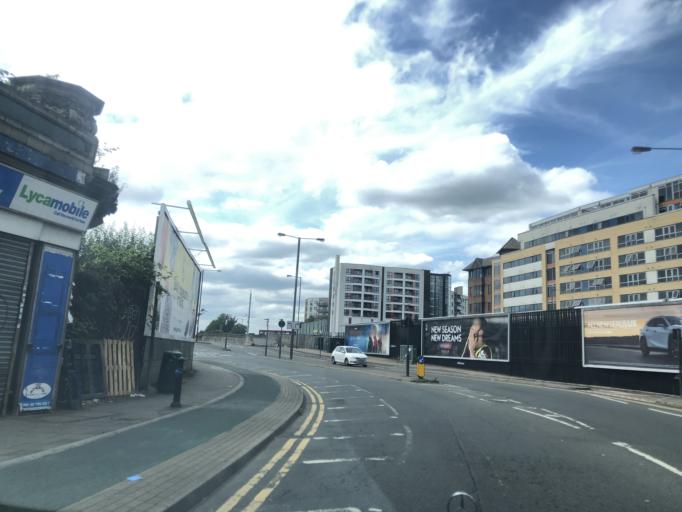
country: GB
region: England
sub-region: Greater London
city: Greenhill
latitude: 51.5795
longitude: -0.3396
